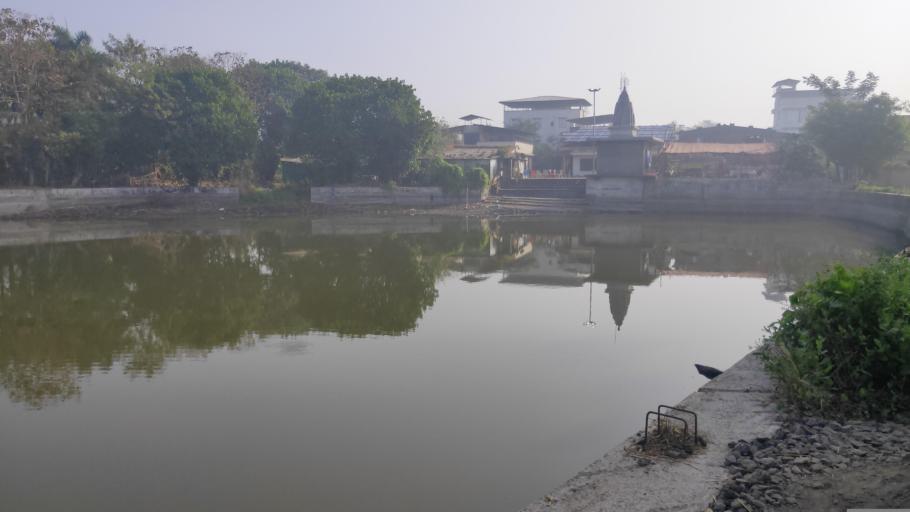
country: IN
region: Maharashtra
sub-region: Thane
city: Bhiwandi
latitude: 19.3526
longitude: 73.0761
